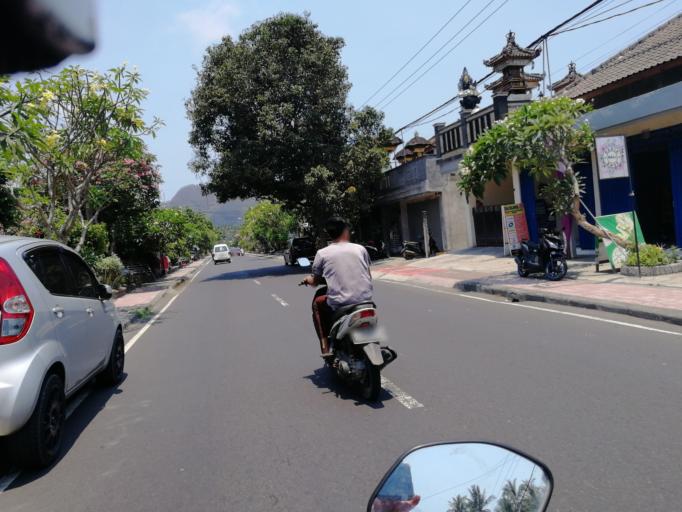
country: ID
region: Bali
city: Banjar Tengah
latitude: -8.4995
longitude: 115.5498
